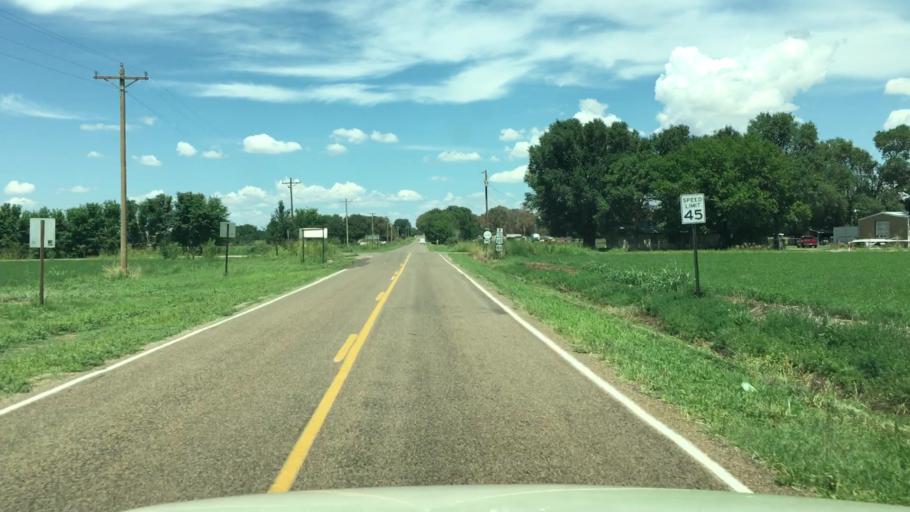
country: US
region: New Mexico
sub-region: De Baca County
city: Fort Sumner
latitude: 34.4334
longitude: -104.1935
